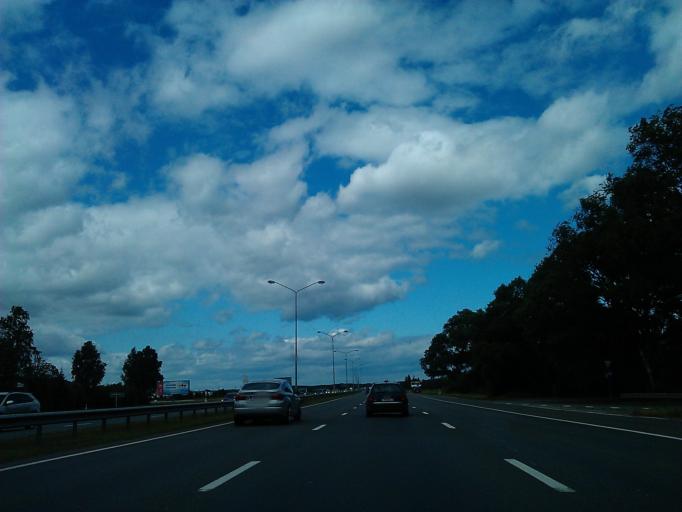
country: LV
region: Babite
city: Pinki
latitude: 56.9558
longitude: 23.9160
